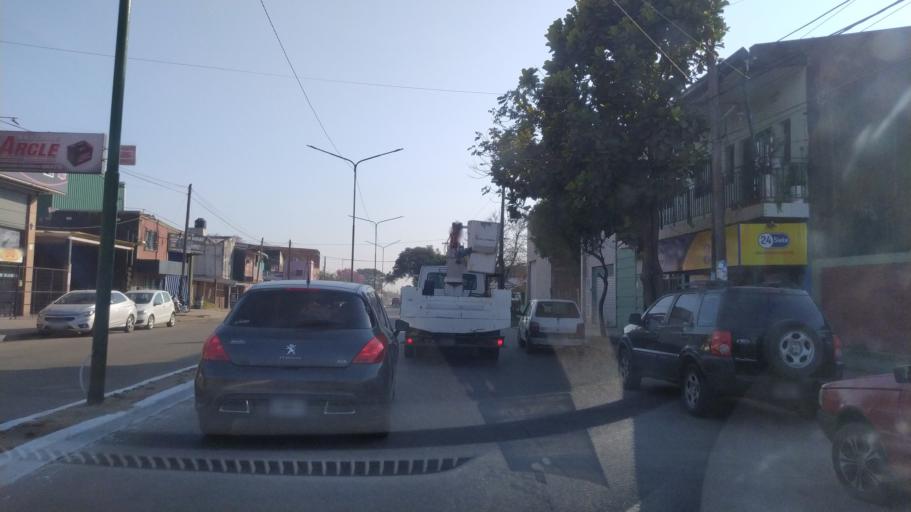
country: AR
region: Corrientes
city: Corrientes
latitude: -27.4908
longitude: -58.8169
